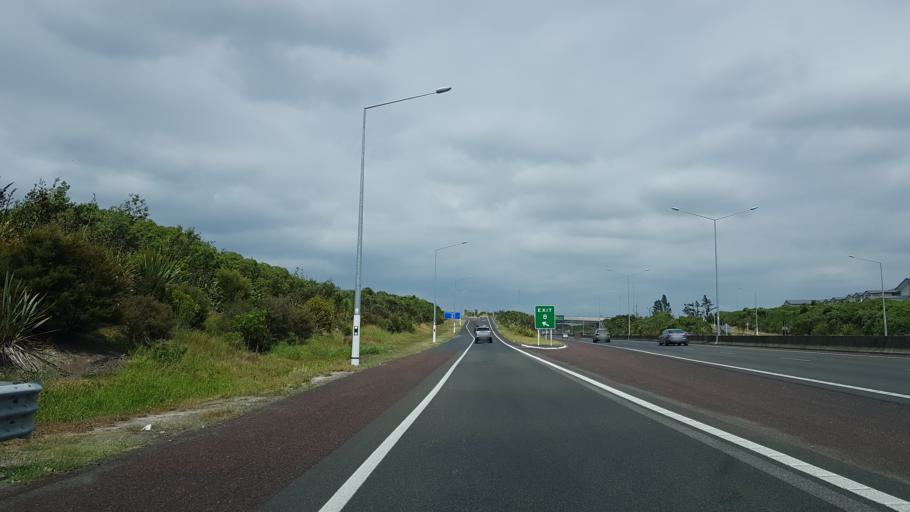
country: NZ
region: Auckland
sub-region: Auckland
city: Rosebank
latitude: -36.7890
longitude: 174.6581
